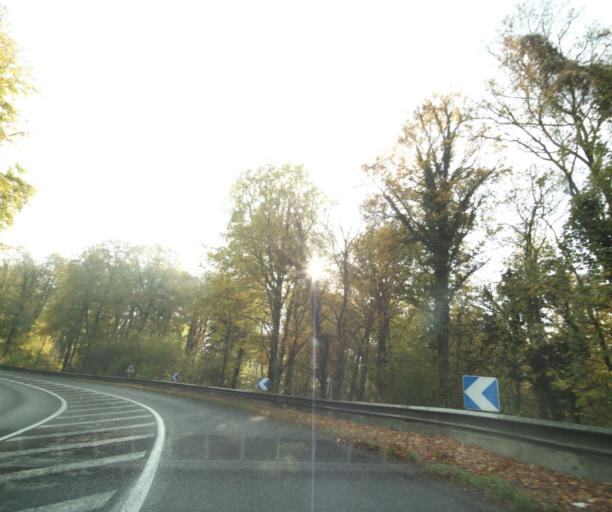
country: FR
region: Lorraine
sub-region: Departement de Meurthe-et-Moselle
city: Briey
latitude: 49.2633
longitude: 5.9246
